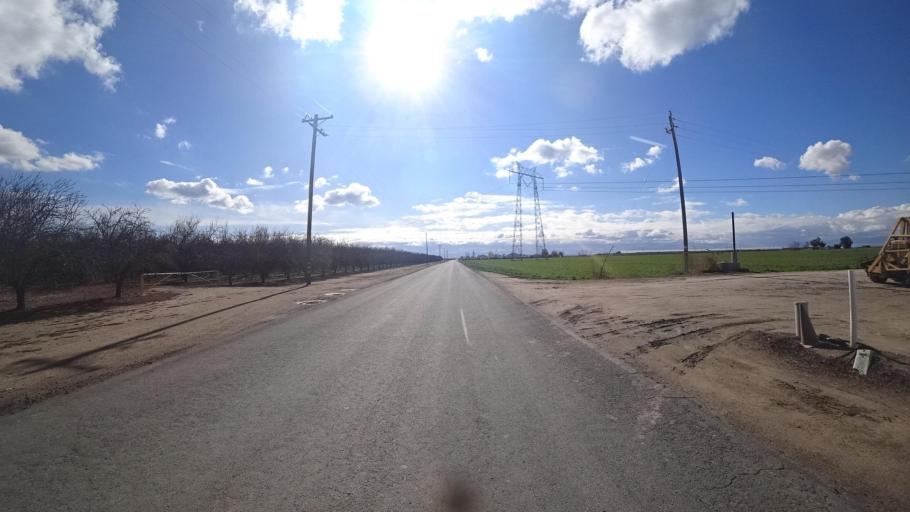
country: US
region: California
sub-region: Kern County
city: Greenfield
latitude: 35.2565
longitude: -119.1284
